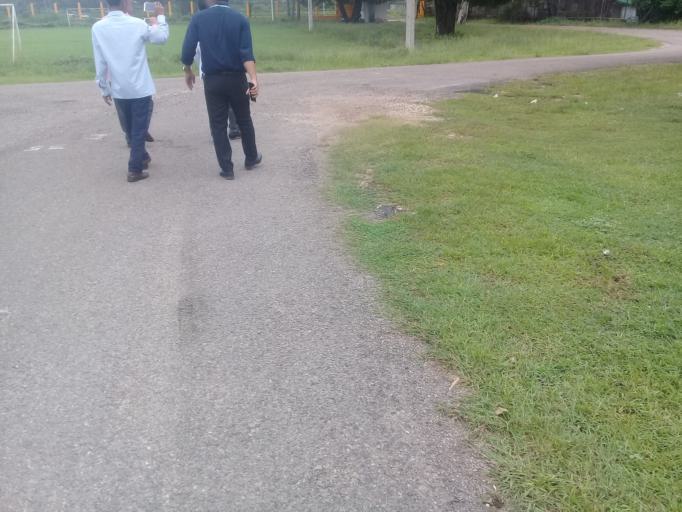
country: TH
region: Nong Khai
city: Nong Khai
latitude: 17.8839
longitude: 102.7136
